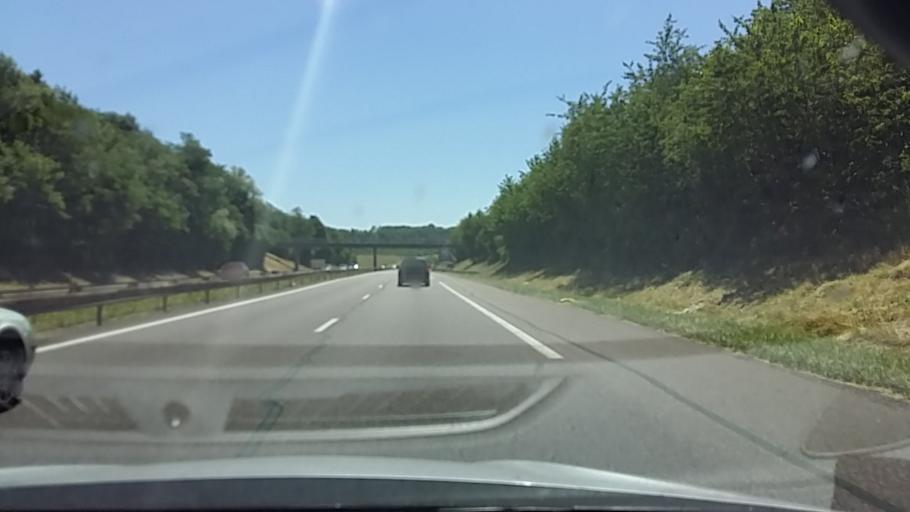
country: FR
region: Lorraine
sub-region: Departement de la Moselle
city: Saint-Julien-les-Metz
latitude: 49.1652
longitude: 6.2513
